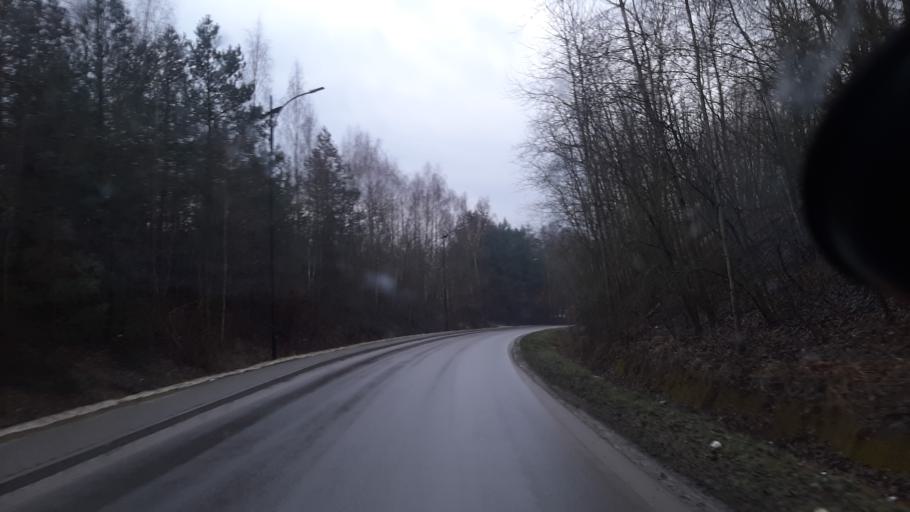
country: PL
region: Lublin Voivodeship
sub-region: Powiat lubelski
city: Lublin
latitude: 51.3192
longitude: 22.5614
